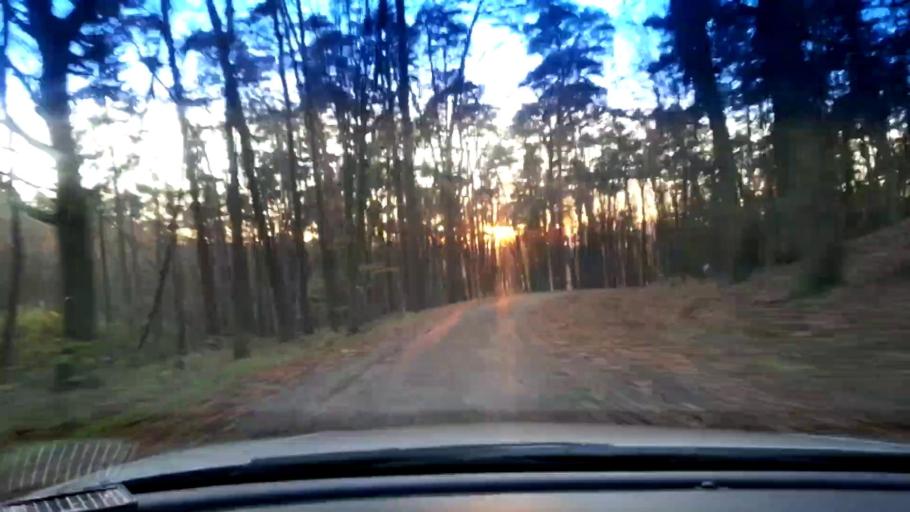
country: DE
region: Bavaria
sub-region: Upper Franconia
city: Zapfendorf
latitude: 50.0296
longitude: 10.9469
